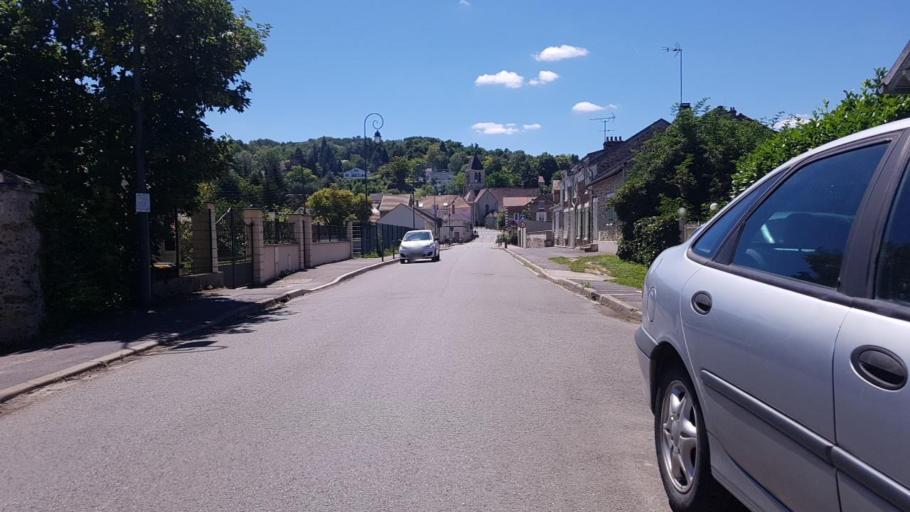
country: FR
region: Ile-de-France
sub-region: Departement de Seine-et-Marne
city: Saint-Jean-les-Deux-Jumeaux
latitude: 48.9533
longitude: 3.0193
